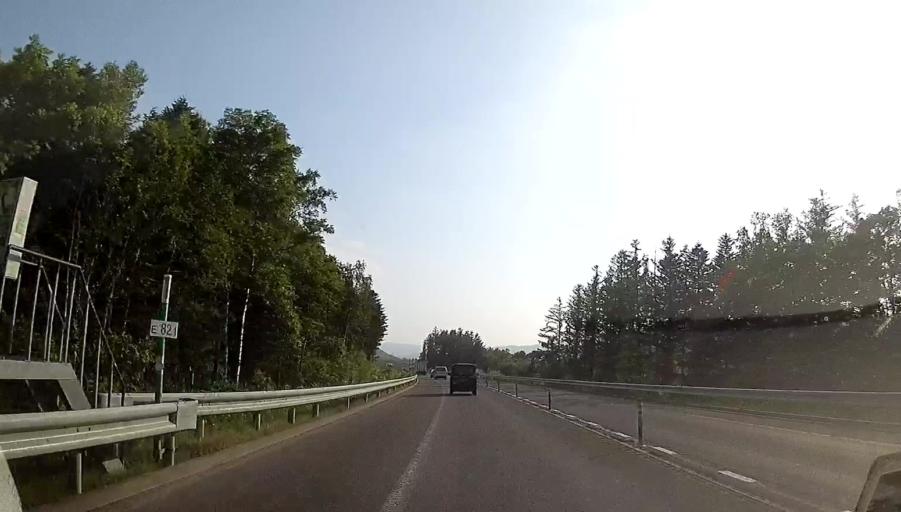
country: JP
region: Hokkaido
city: Shimo-furano
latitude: 43.0202
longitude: 142.4381
